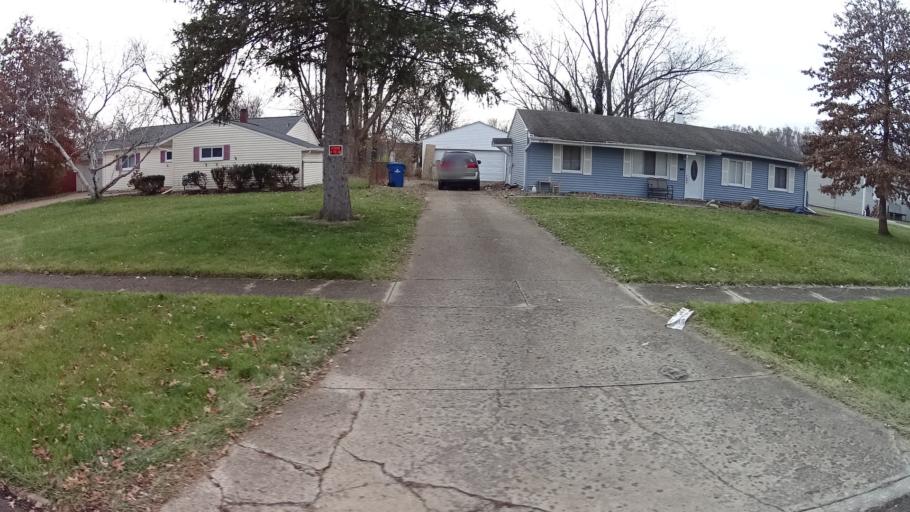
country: US
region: Ohio
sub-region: Lorain County
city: North Ridgeville
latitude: 41.3840
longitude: -81.9926
